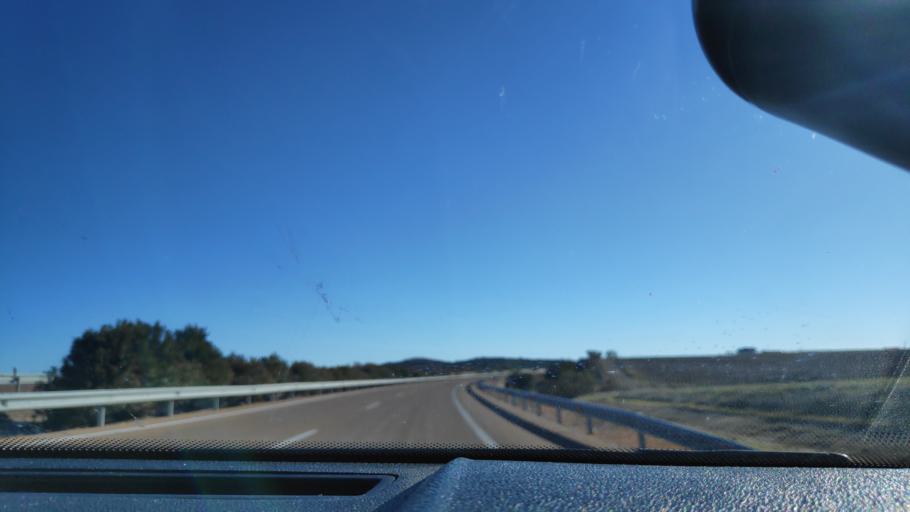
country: ES
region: Extremadura
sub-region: Provincia de Badajoz
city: Los Santos de Maimona
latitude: 38.4499
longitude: -6.3458
